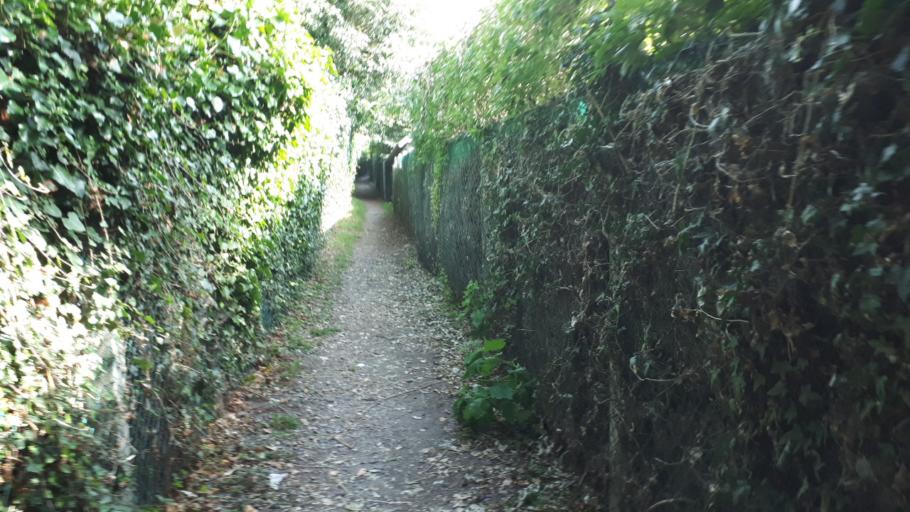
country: FR
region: Brittany
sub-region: Departement du Finistere
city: Carantec
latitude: 48.6703
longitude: -3.8992
